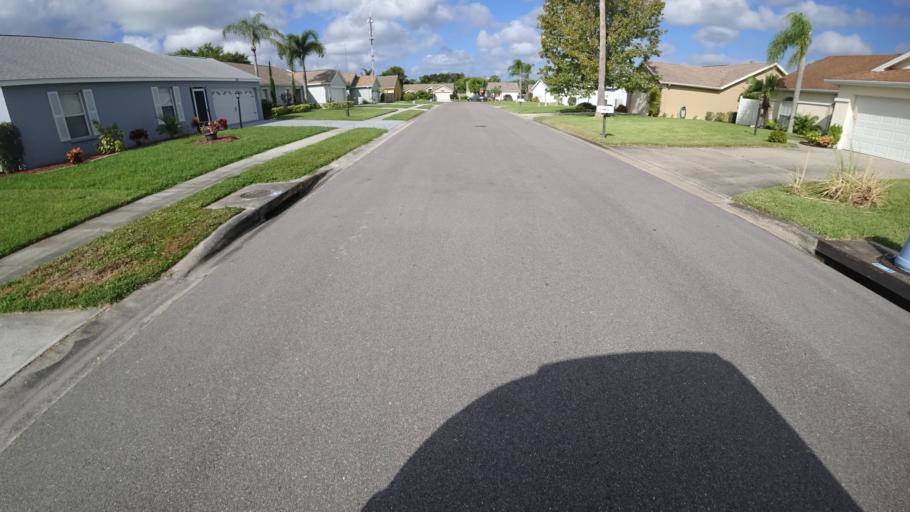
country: US
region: Florida
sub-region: Manatee County
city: Memphis
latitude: 27.5460
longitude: -82.5702
